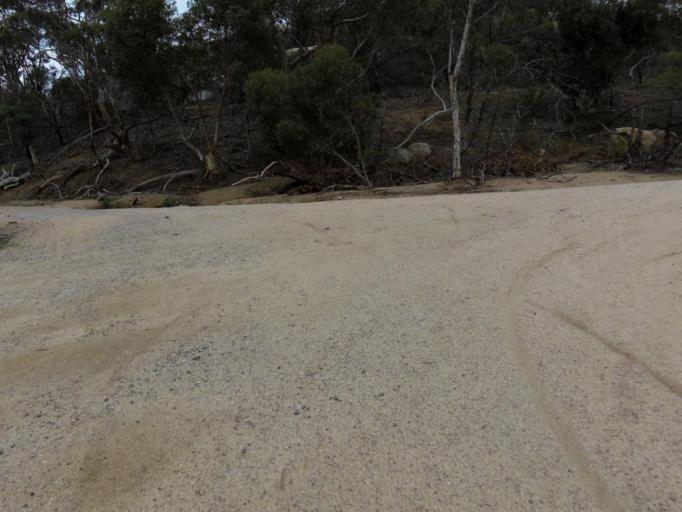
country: AU
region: Victoria
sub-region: Wyndham
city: Little River
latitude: -37.9324
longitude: 144.4419
